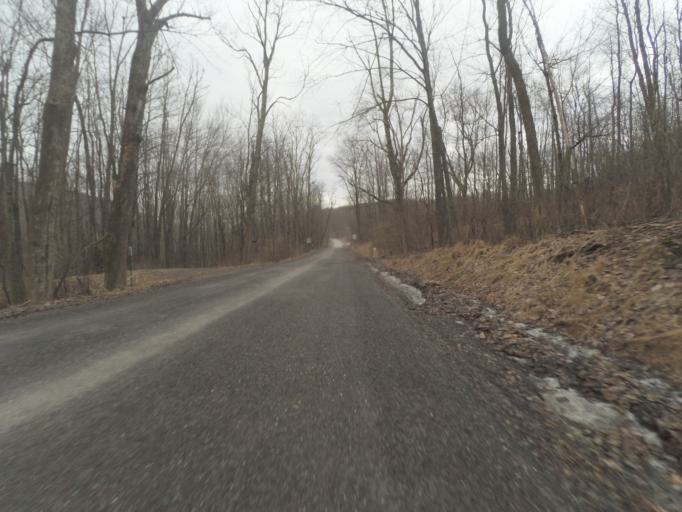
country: US
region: Pennsylvania
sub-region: Centre County
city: Stormstown
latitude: 40.8738
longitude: -78.0072
